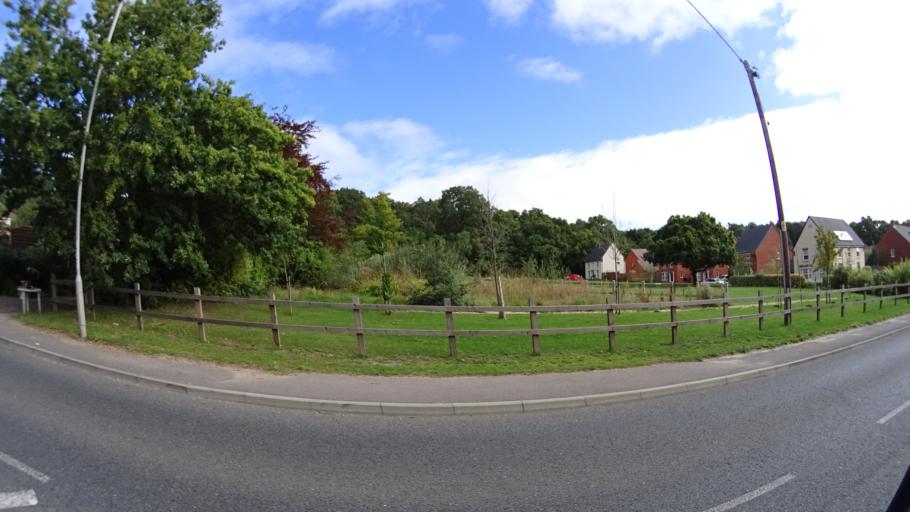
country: GB
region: England
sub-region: Dorset
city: Ferndown
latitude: 50.7847
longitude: -1.8977
